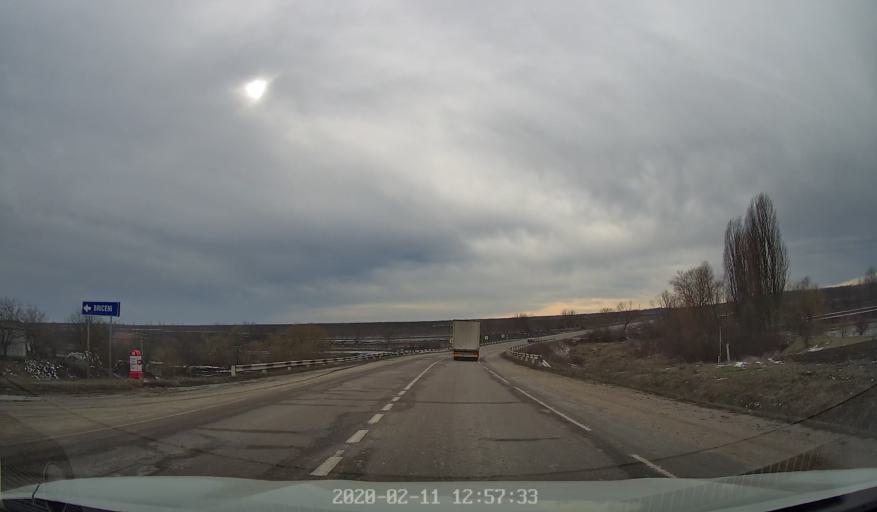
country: MD
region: Briceni
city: Briceni
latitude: 48.3398
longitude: 27.0661
